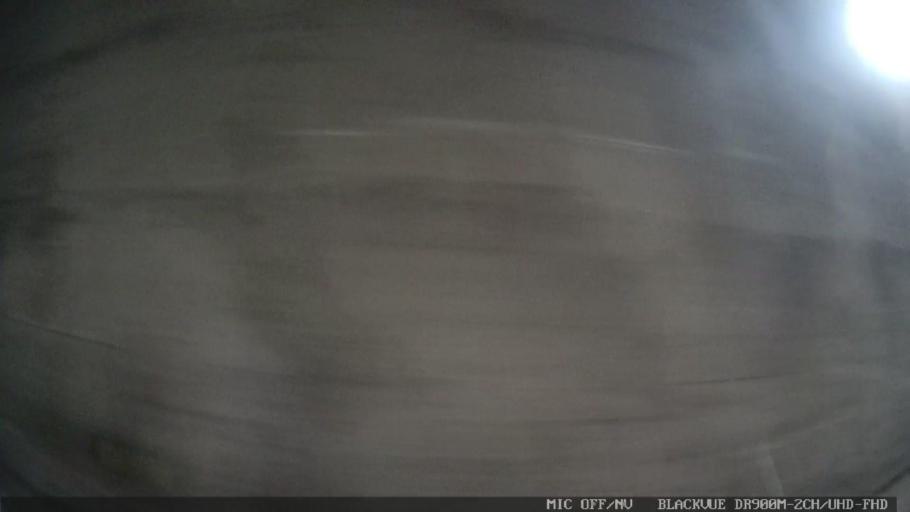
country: BR
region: Sao Paulo
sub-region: Cubatao
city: Cubatao
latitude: -23.8941
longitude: -46.5068
